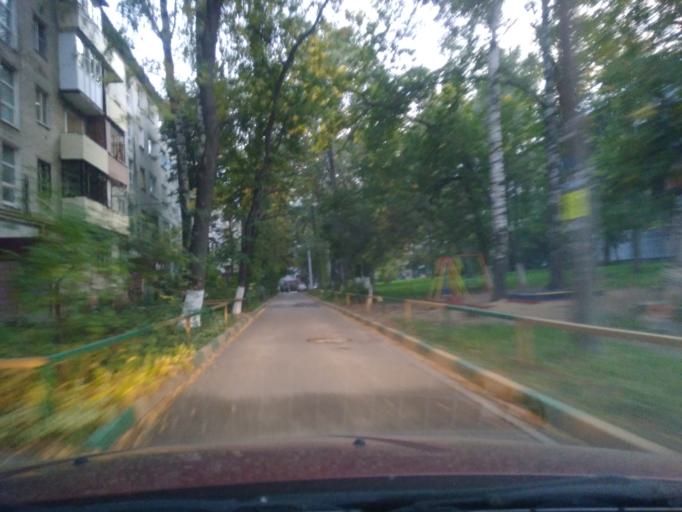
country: RU
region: Nizjnij Novgorod
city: Afonino
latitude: 56.2915
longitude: 44.0458
